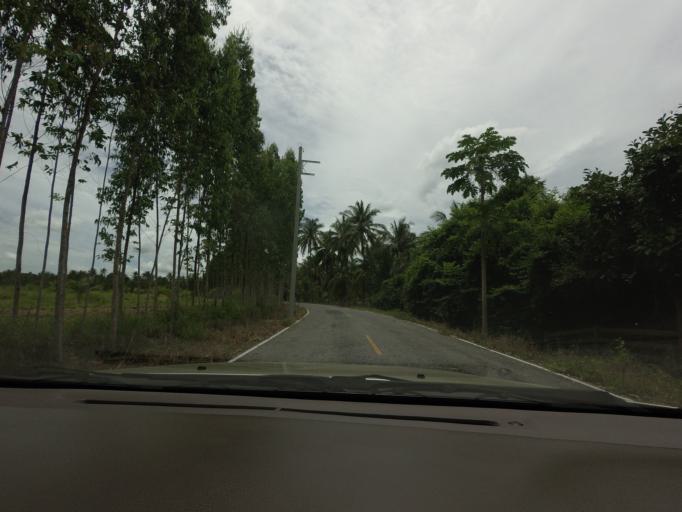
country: TH
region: Chon Buri
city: Ban Bueng
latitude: 13.2231
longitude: 101.0410
